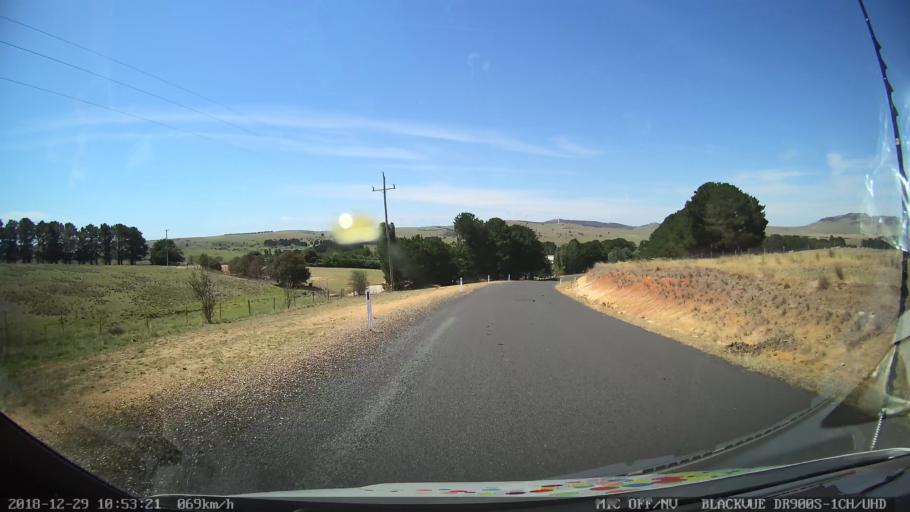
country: AU
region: New South Wales
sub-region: Palerang
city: Bungendore
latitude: -35.1077
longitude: 149.5219
